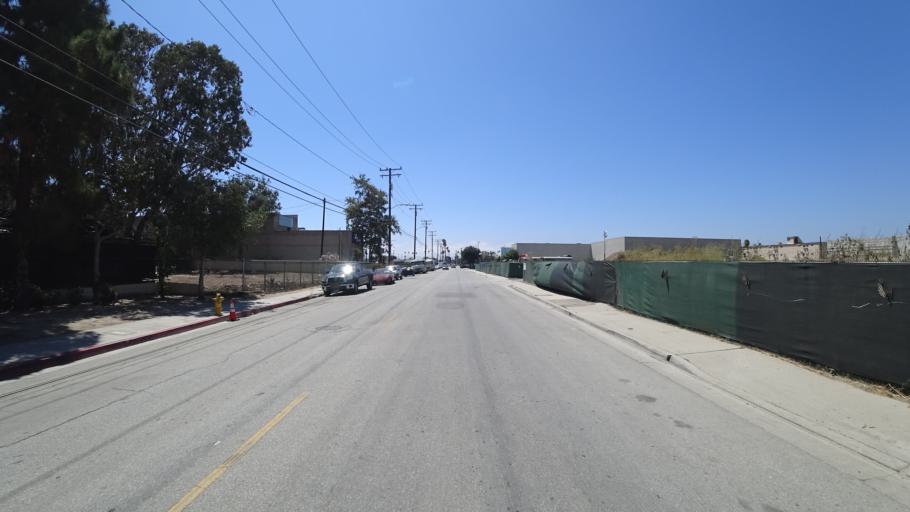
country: US
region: California
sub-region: Los Angeles County
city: Lennox
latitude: 33.9437
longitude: -118.3407
